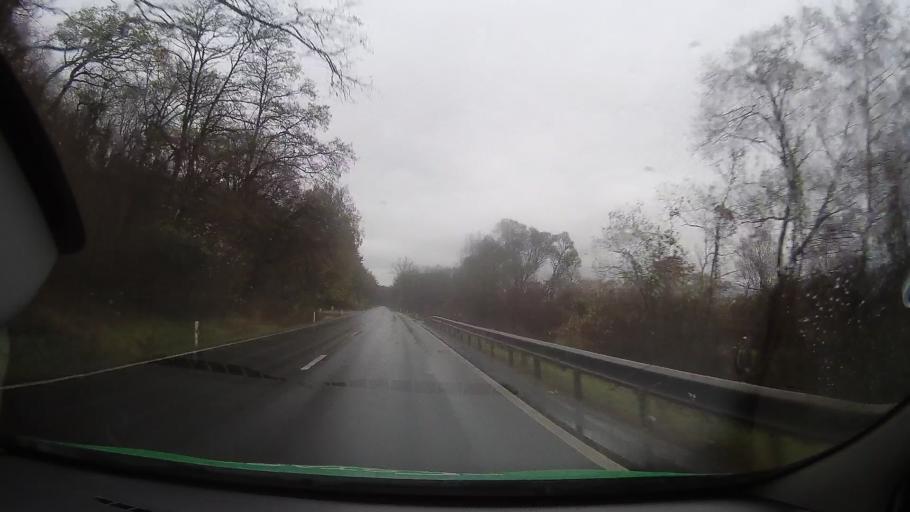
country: RO
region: Mures
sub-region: Comuna Brancovenesti
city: Brancovenesti
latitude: 46.8706
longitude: 24.7718
